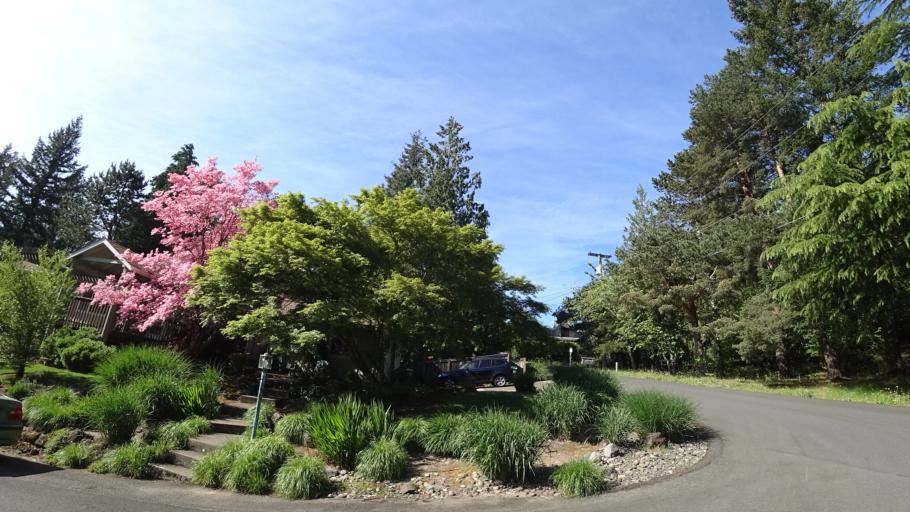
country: US
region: Oregon
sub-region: Washington County
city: West Slope
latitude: 45.4976
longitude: -122.7504
